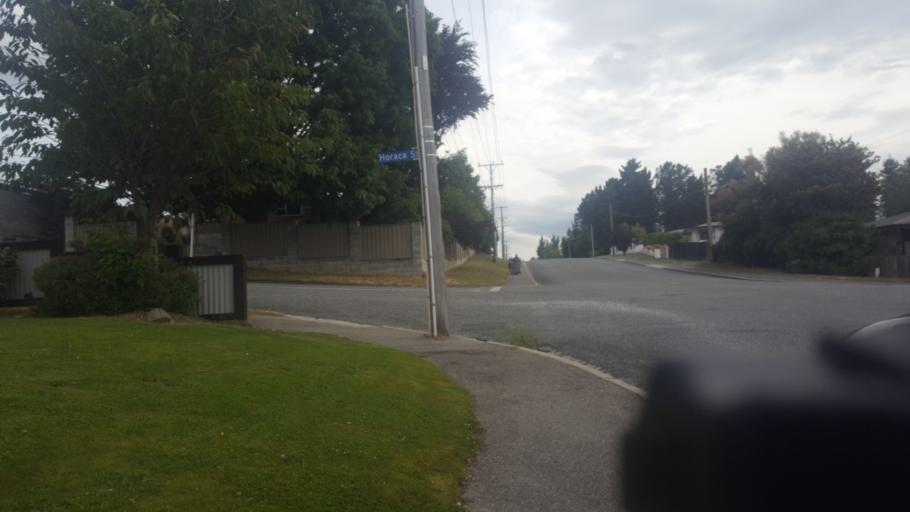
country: NZ
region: Otago
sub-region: Queenstown-Lakes District
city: Wanaka
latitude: -45.0441
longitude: 169.2070
